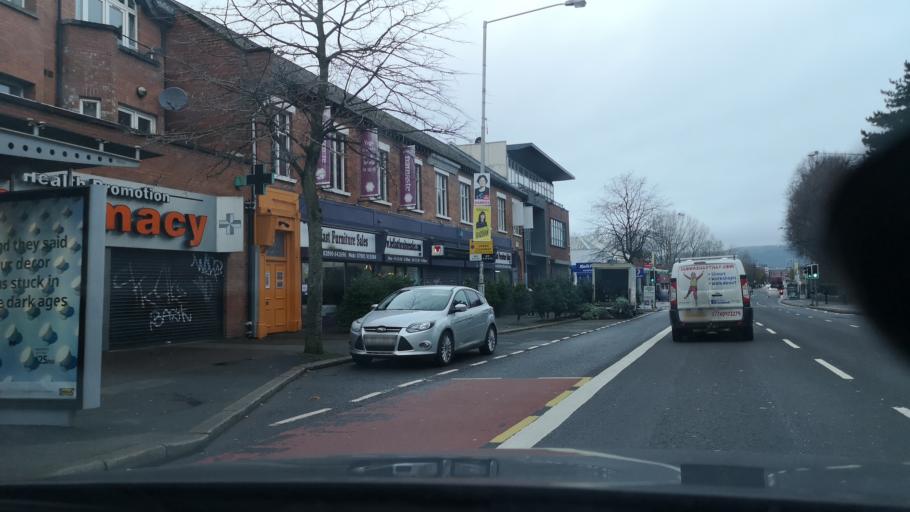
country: GB
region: Northern Ireland
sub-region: City of Belfast
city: Belfast
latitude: 54.5808
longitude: -5.9210
